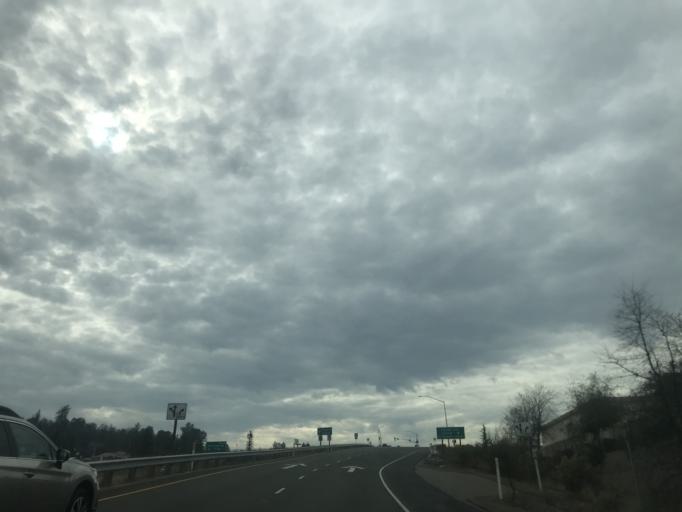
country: US
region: California
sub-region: El Dorado County
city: Diamond Springs
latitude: 38.7138
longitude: -120.8381
